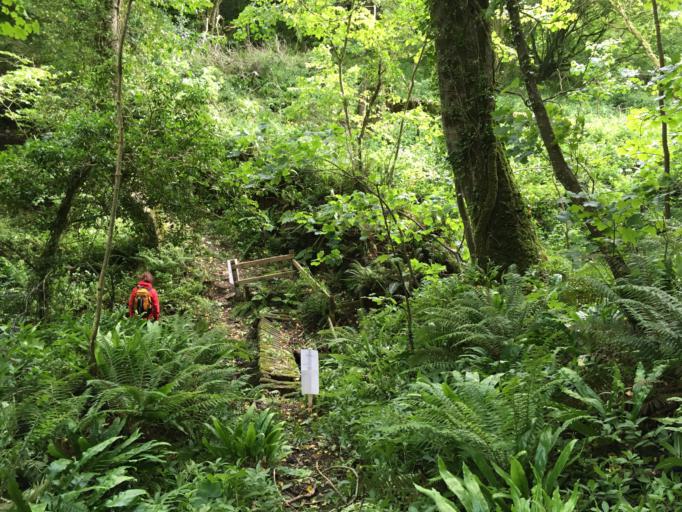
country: GB
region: England
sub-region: Cornwall
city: Flexbury
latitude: 50.9048
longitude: -4.5528
